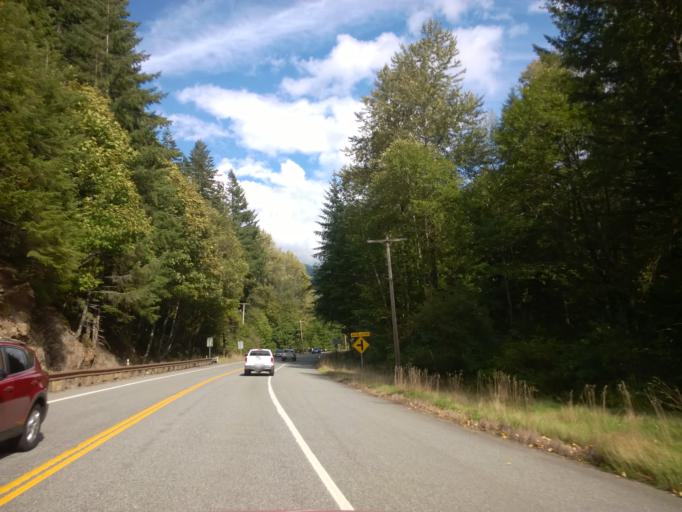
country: US
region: Washington
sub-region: Snohomish County
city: Gold Bar
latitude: 47.7144
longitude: -121.3470
